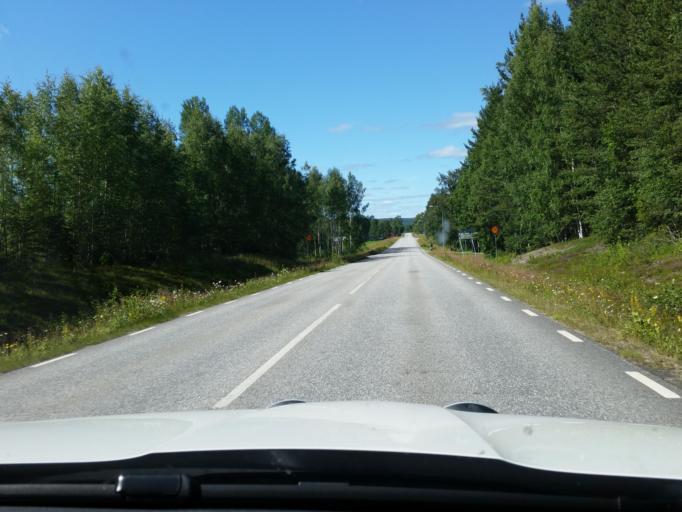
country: SE
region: Norrbotten
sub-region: Pitea Kommun
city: Hortlax
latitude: 65.2677
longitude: 21.3204
